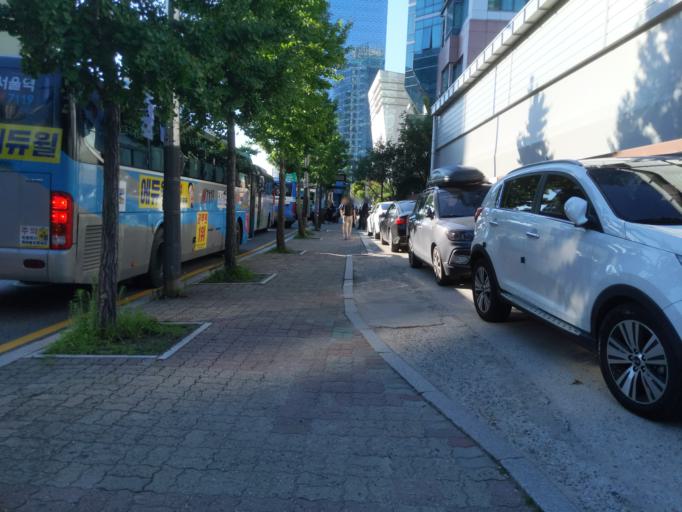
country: KR
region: Seoul
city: Seoul
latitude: 37.5646
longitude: 126.9680
